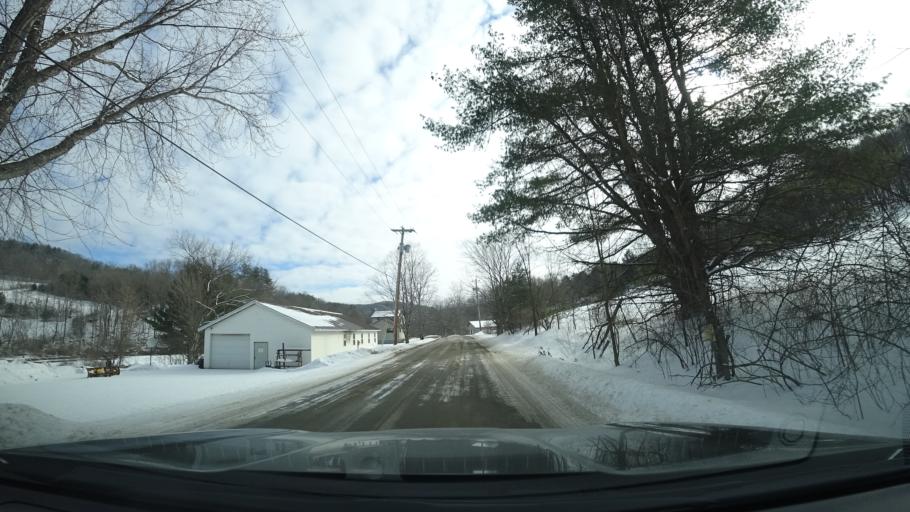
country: US
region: New York
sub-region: Washington County
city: Greenwich
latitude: 43.2282
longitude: -73.3669
